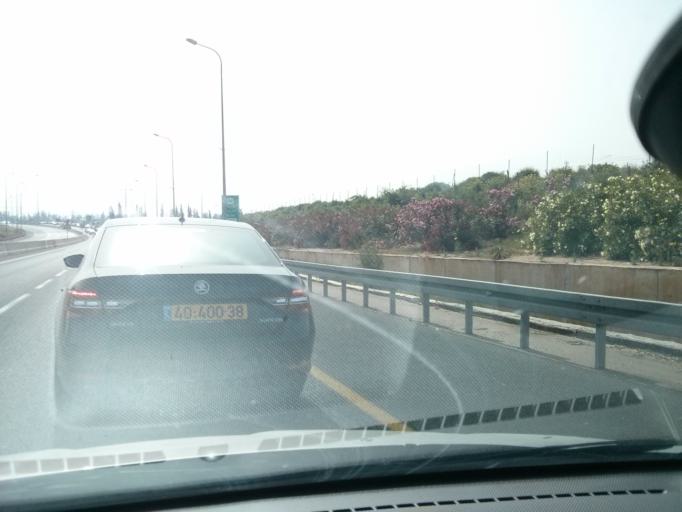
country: IL
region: Central District
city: Even Yehuda
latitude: 32.2549
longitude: 34.8830
